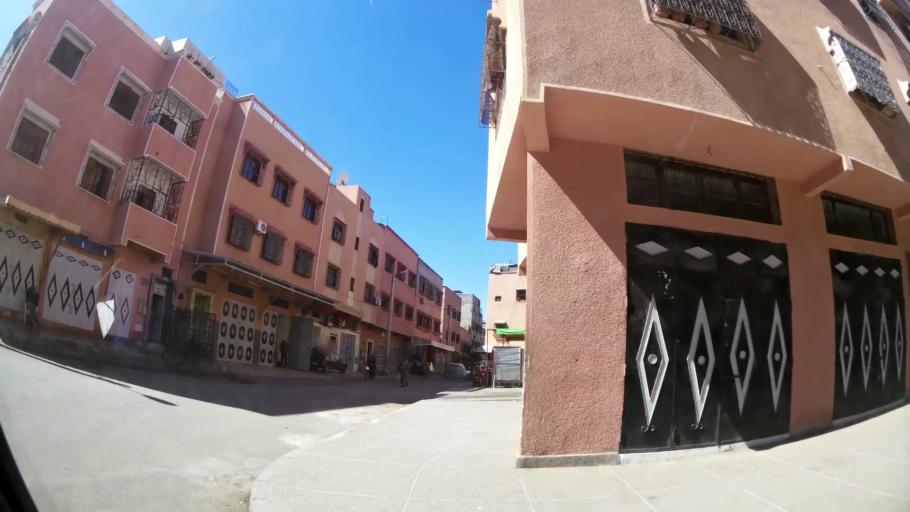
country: MA
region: Marrakech-Tensift-Al Haouz
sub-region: Marrakech
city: Marrakesh
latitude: 31.6484
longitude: -7.9811
